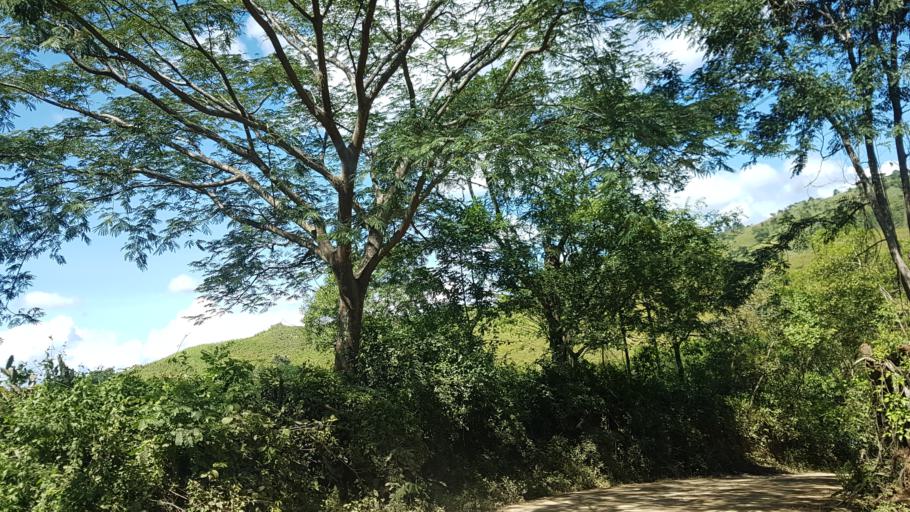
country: HN
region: El Paraiso
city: Santa Cruz
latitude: 13.7313
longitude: -86.6824
